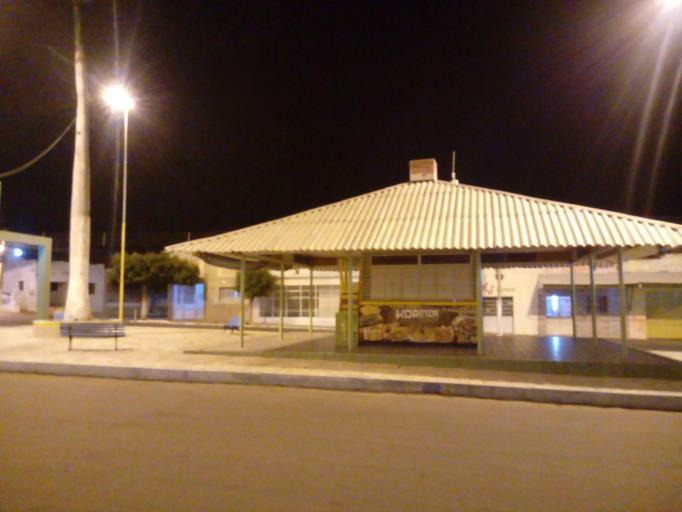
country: BR
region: Pernambuco
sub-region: Tabira
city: Tabira
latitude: -7.5149
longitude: -37.6403
